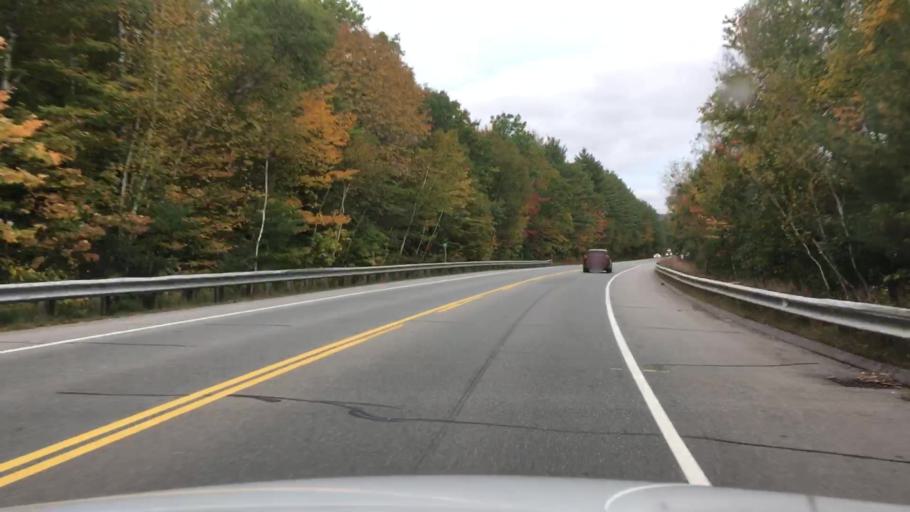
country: US
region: New Hampshire
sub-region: Coos County
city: Gorham
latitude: 44.3852
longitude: -71.0234
